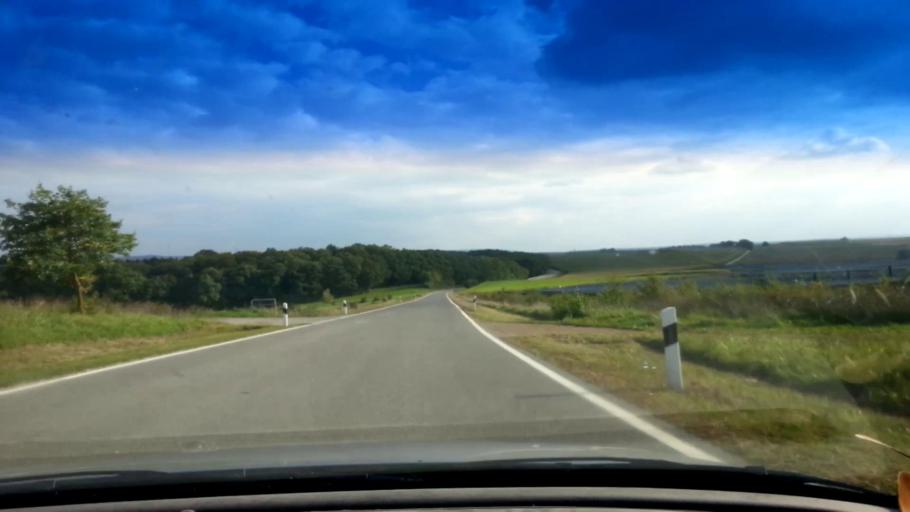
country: DE
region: Bavaria
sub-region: Upper Franconia
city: Zapfendorf
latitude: 49.9841
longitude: 10.9658
